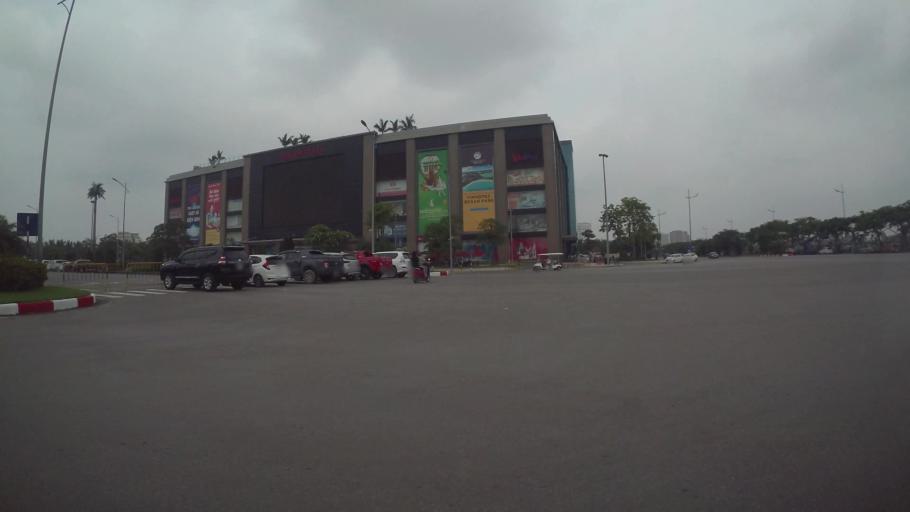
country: VN
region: Ha Noi
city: Trau Quy
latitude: 21.0504
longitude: 105.9174
